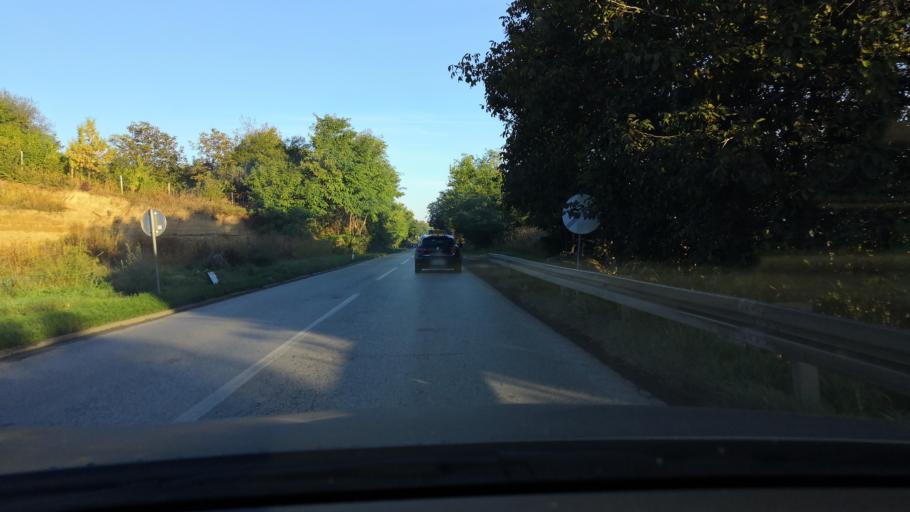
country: RS
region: Autonomna Pokrajina Vojvodina
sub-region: Juznobacki Okrug
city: Petrovaradin
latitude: 45.2210
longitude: 19.9024
